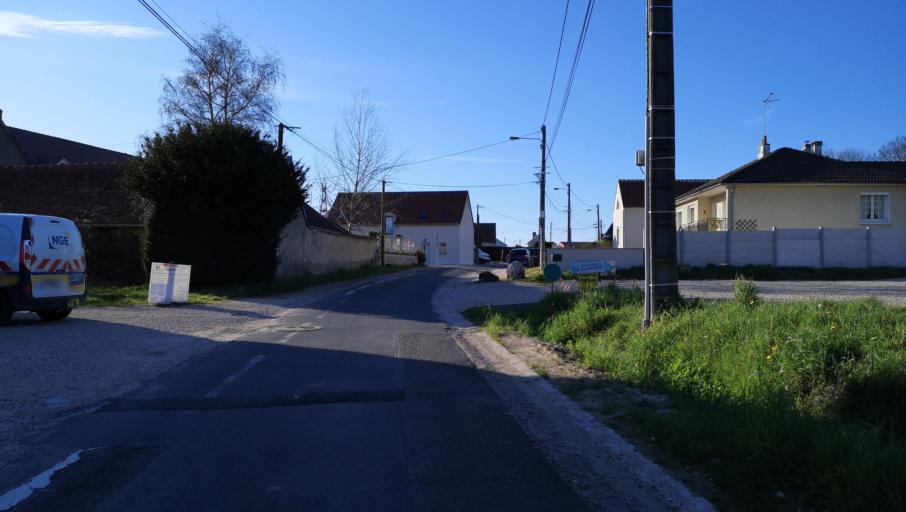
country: FR
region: Centre
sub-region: Departement du Loiret
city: Saint-Jean-de-Braye
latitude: 47.9204
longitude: 1.9761
